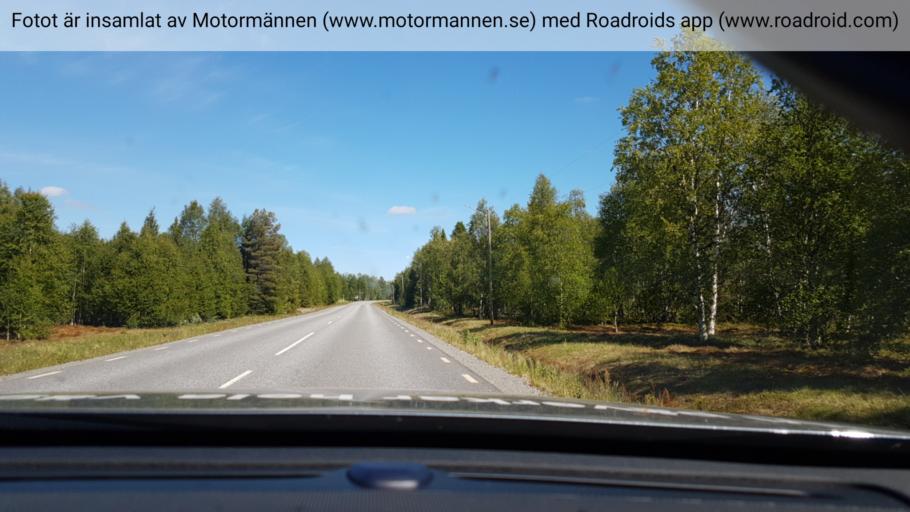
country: SE
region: Vaesterbotten
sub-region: Storumans Kommun
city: Storuman
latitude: 64.7030
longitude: 17.1274
